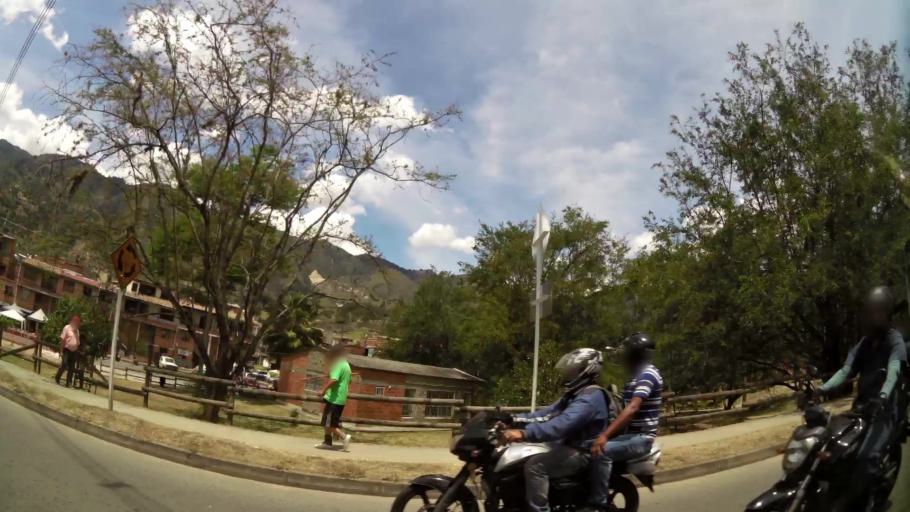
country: CO
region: Antioquia
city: Bello
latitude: 6.3453
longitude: -75.5690
